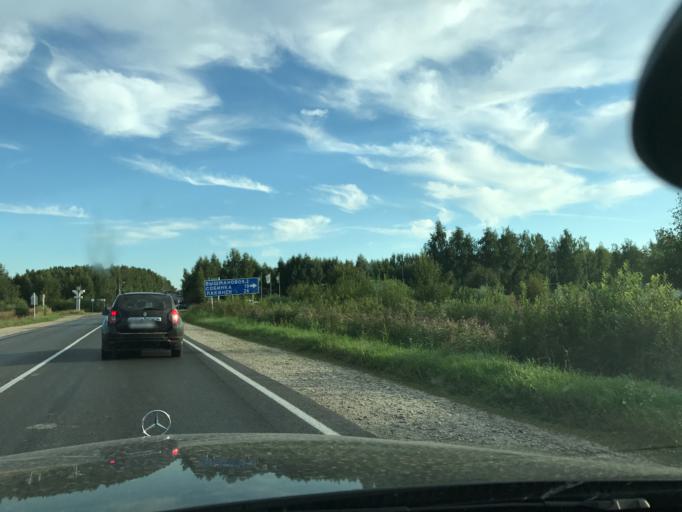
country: RU
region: Vladimir
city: Raduzhnyy
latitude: 56.0080
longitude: 40.3065
